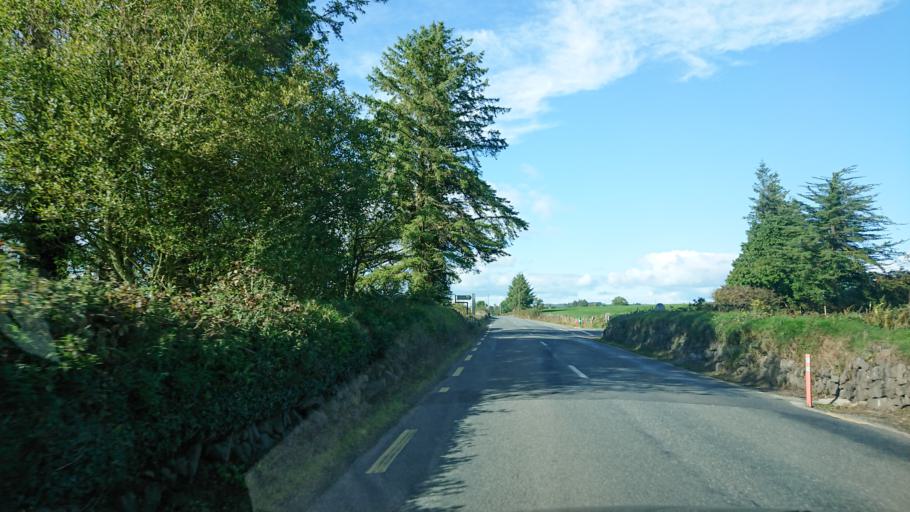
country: IE
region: Munster
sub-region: Waterford
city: Dungarvan
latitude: 52.1860
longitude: -7.6952
